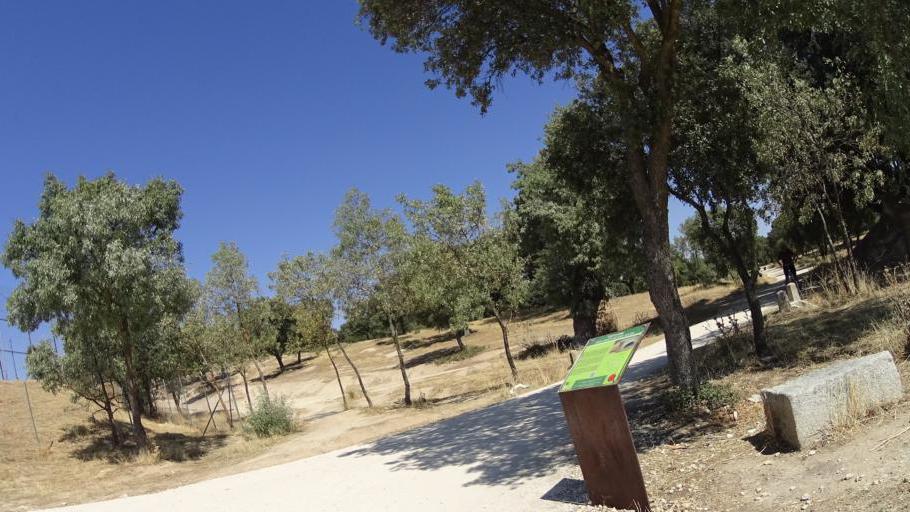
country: ES
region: Madrid
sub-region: Provincia de Madrid
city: Boadilla del Monte
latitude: 40.4187
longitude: -3.8589
